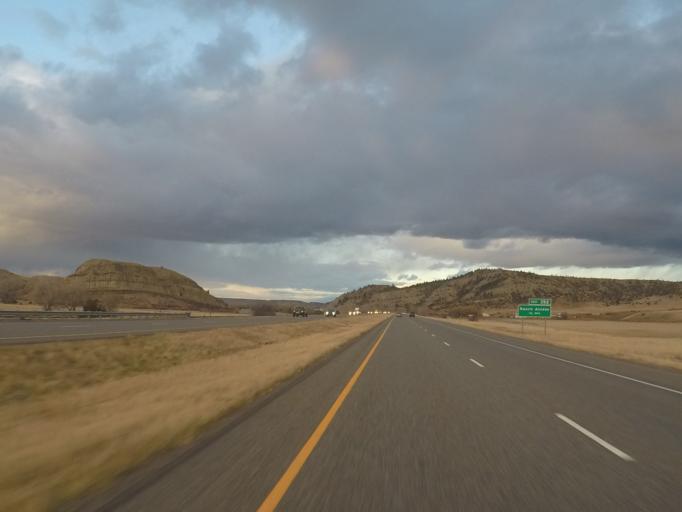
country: US
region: Montana
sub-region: Park County
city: Livingston
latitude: 45.7200
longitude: -110.2537
